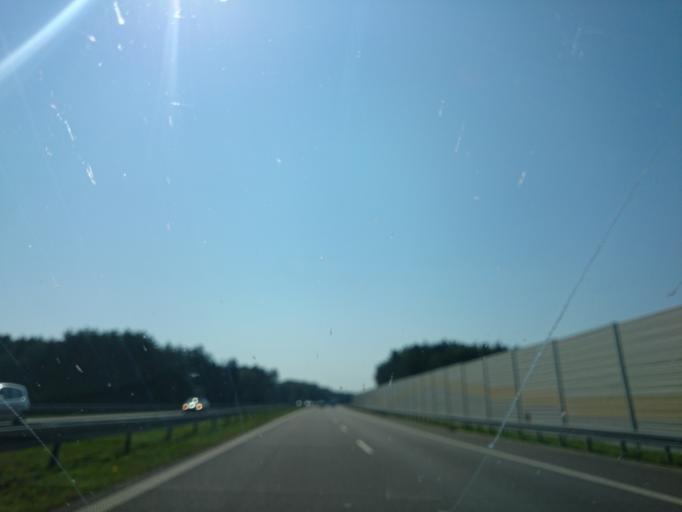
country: PL
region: West Pomeranian Voivodeship
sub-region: Powiat mysliborski
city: Nowogrodek Pomorski
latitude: 52.8627
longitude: 15.0340
